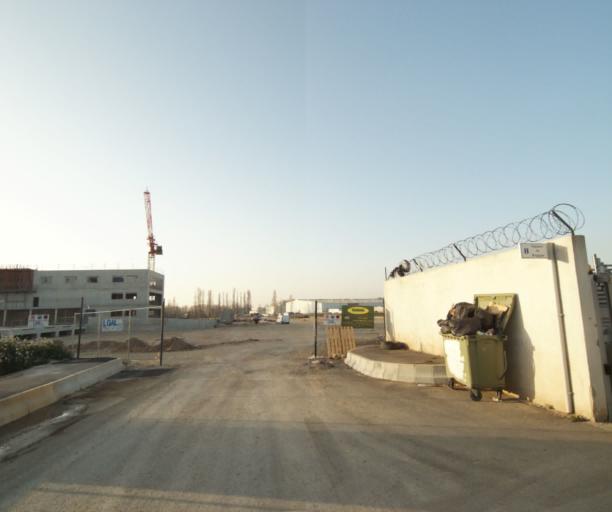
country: FR
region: Provence-Alpes-Cote d'Azur
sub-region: Departement des Bouches-du-Rhone
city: Saint-Victoret
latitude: 43.4197
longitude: 5.2628
